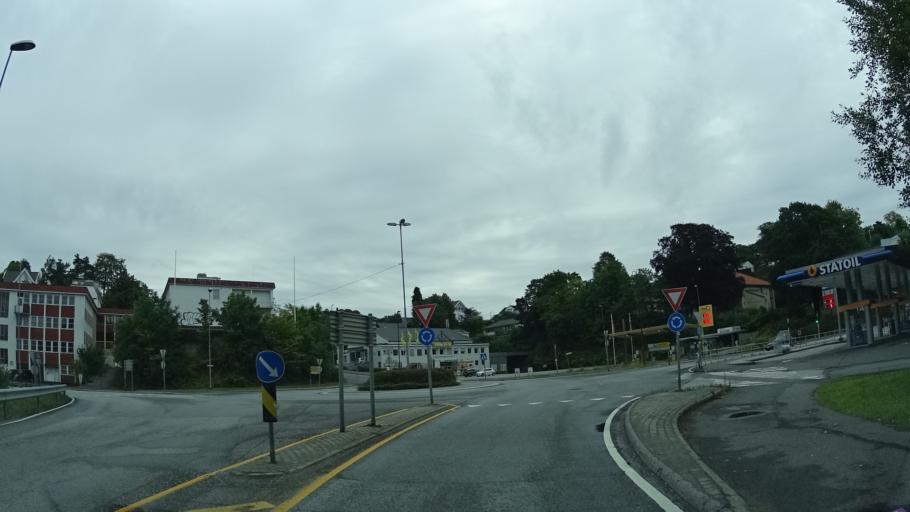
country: NO
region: Aust-Agder
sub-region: Arendal
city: Arendal
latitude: 58.4579
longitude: 8.7530
